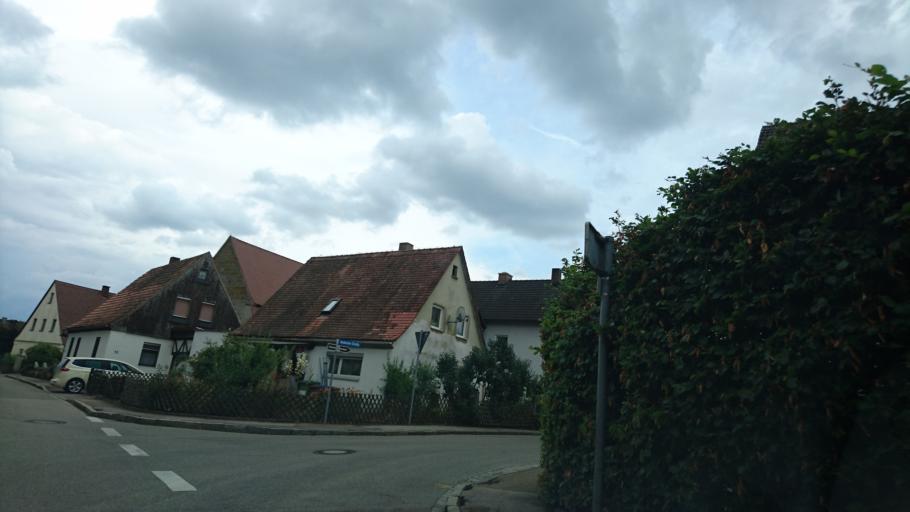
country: DE
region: Bavaria
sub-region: Regierungsbezirk Mittelfranken
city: Heideck
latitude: 49.1900
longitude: 11.1084
